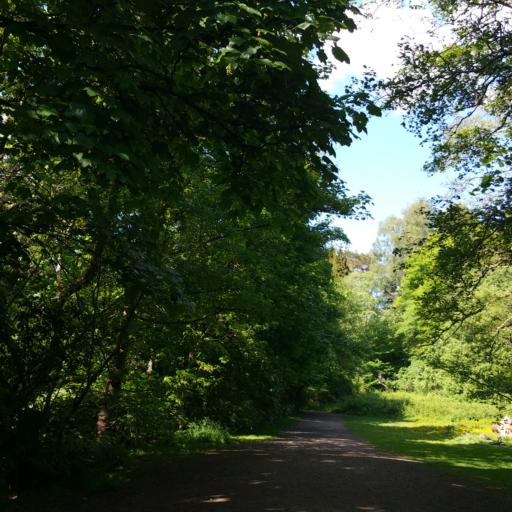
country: GB
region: Scotland
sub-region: East Dunbartonshire
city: Milngavie
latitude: 55.9482
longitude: -4.3219
